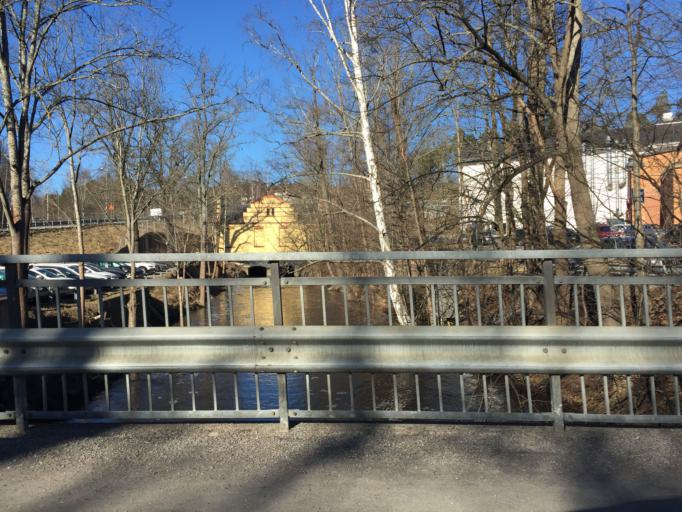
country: SE
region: OEstergoetland
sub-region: Finspangs Kommun
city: Finspang
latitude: 58.7108
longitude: 15.7747
